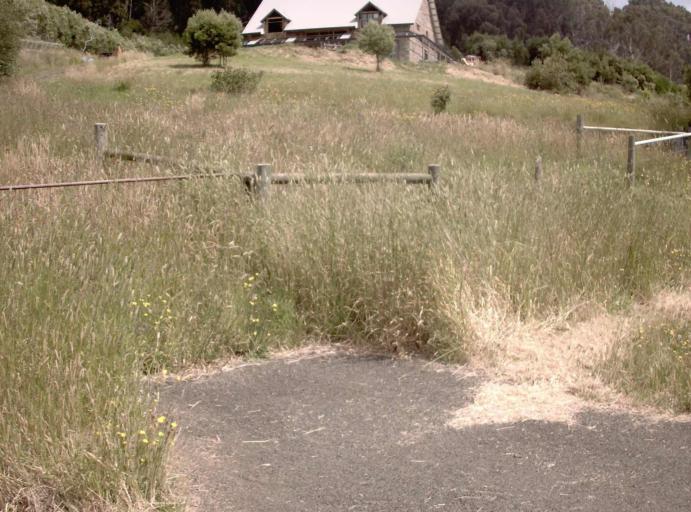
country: AU
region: Victoria
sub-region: Latrobe
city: Traralgon
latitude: -38.3409
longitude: 146.5727
